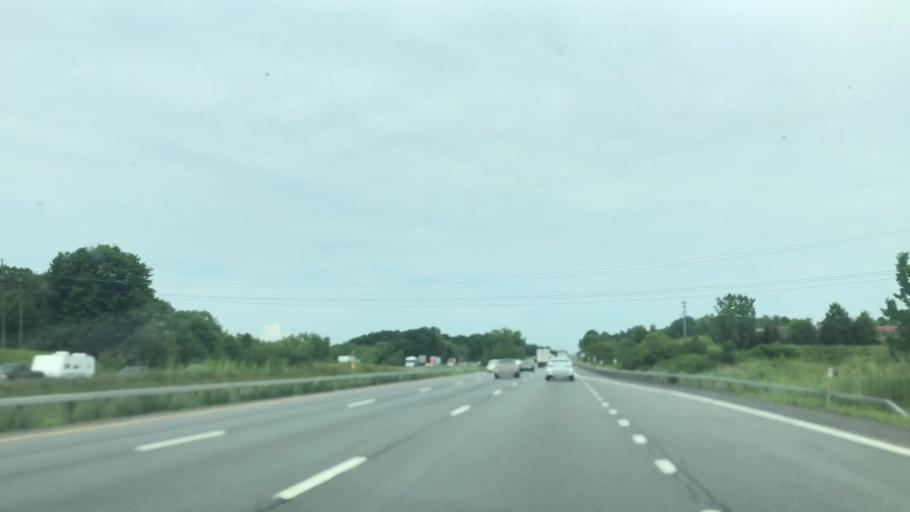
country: US
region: New York
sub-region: Albany County
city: Cohoes
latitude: 42.7689
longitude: -73.7614
